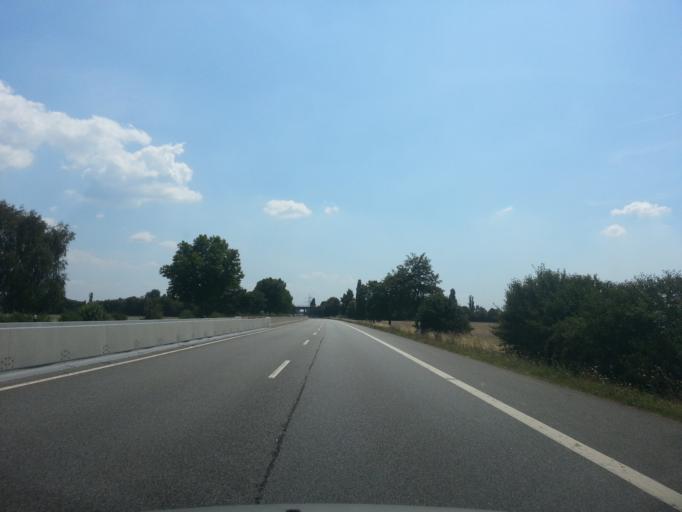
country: DE
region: Hesse
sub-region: Regierungsbezirk Darmstadt
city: Burstadt
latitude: 49.6293
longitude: 8.4552
